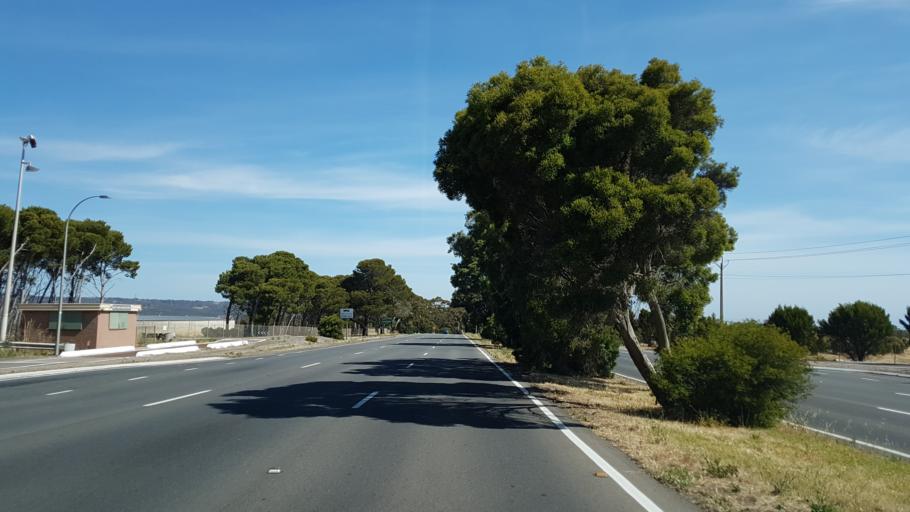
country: AU
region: South Australia
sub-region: Onkaparinga
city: Bedford Park
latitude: -35.0566
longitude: 138.5598
